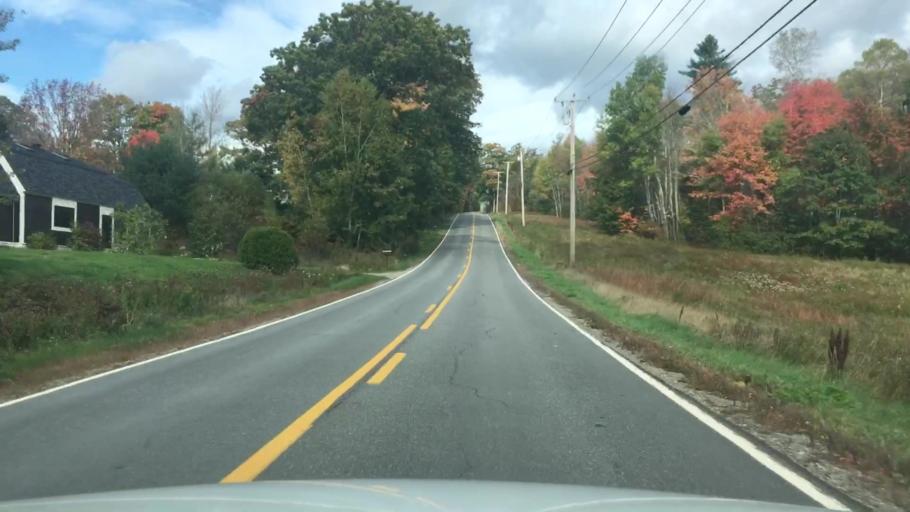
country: US
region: Maine
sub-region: Knox County
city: Hope
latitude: 44.3005
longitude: -69.1102
